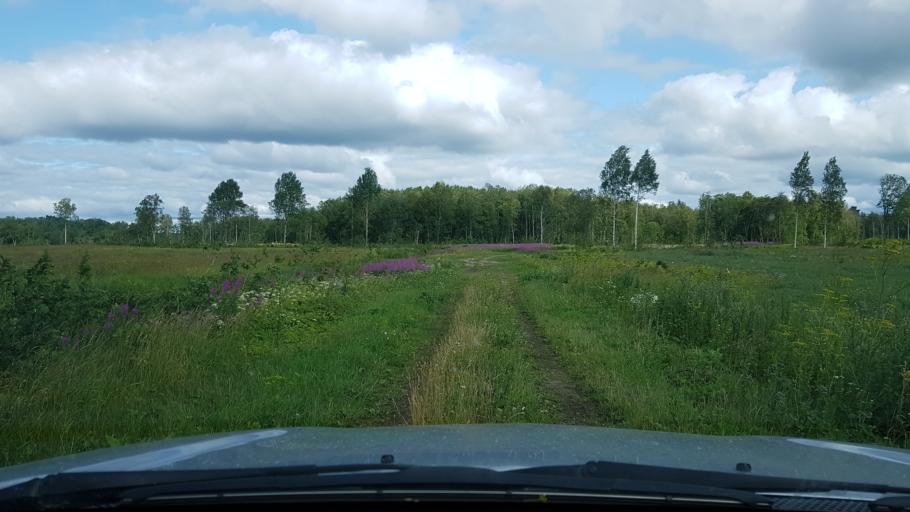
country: EE
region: Ida-Virumaa
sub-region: Narva-Joesuu linn
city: Narva-Joesuu
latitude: 59.3832
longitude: 27.9499
